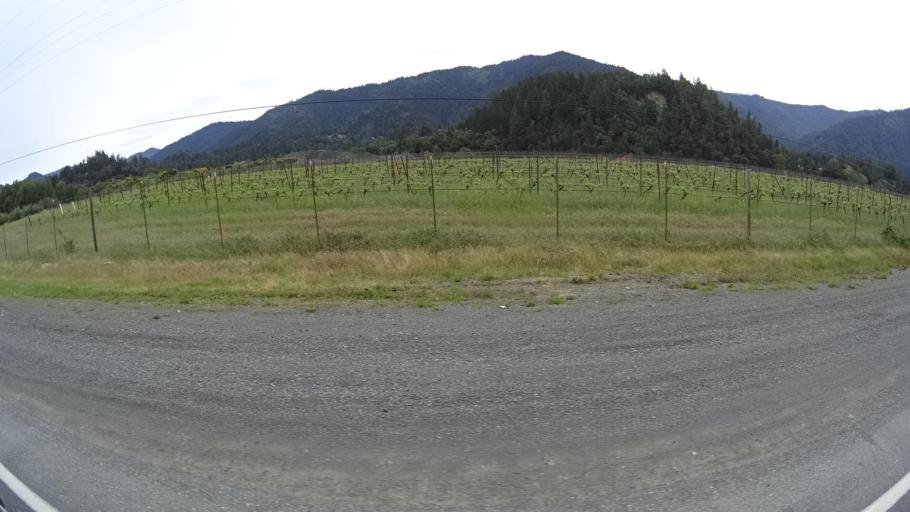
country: US
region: California
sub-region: Humboldt County
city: Willow Creek
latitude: 40.9511
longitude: -123.6395
